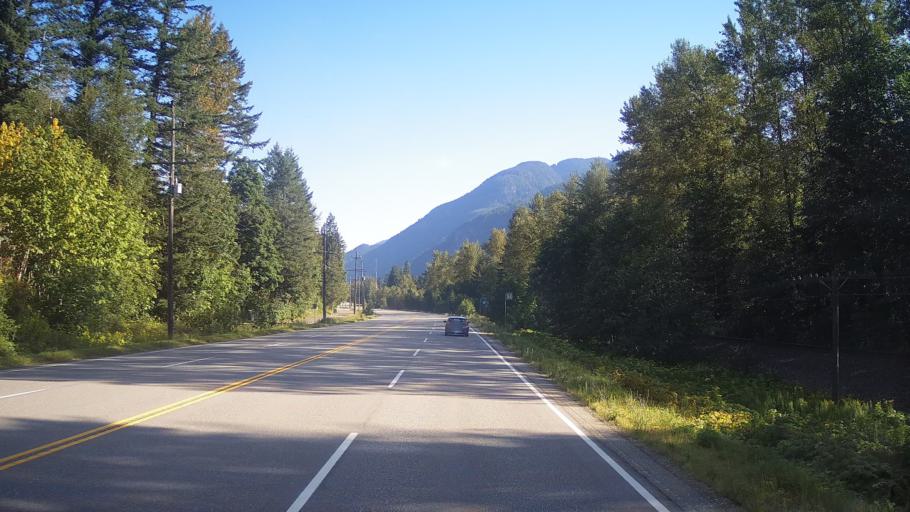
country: CA
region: British Columbia
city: Hope
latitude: 49.4840
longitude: -121.4219
